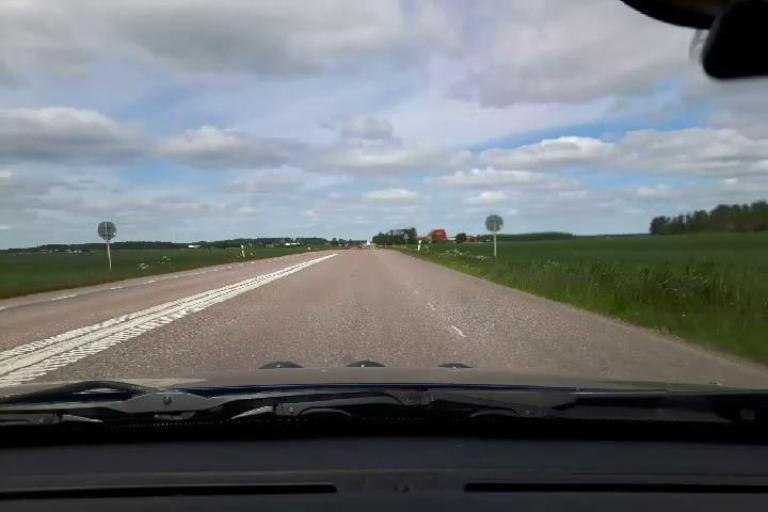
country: SE
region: Uppsala
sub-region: Uppsala Kommun
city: Gamla Uppsala
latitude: 59.9132
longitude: 17.6063
